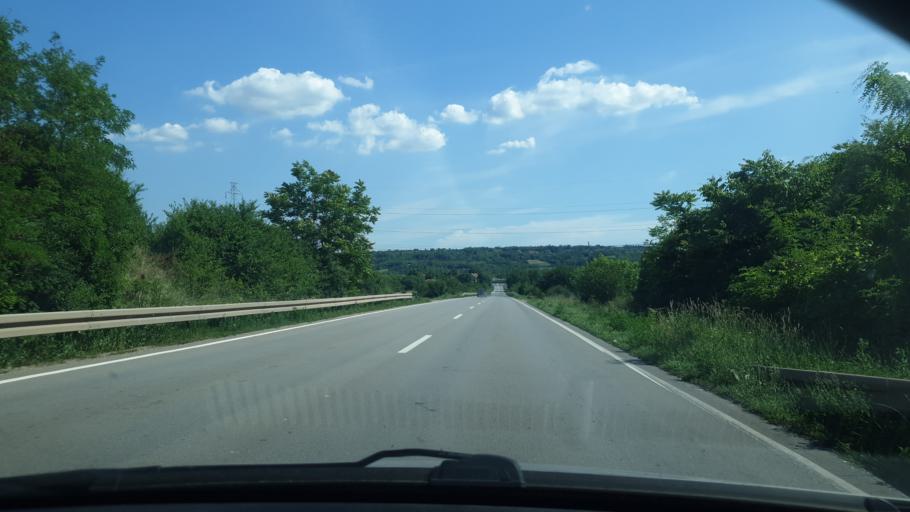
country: RS
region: Central Serbia
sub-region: Podunavski Okrug
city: Smederevo
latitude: 44.5976
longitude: 20.9560
